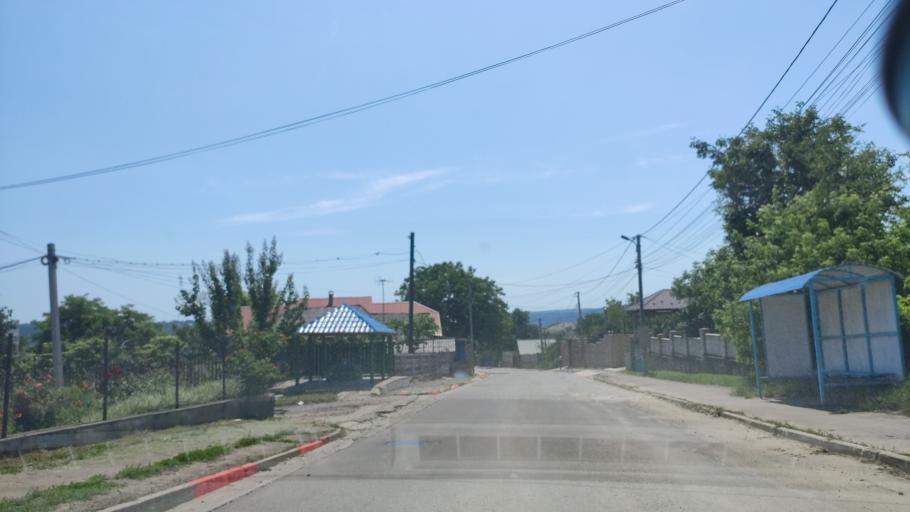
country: MD
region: Raionul Soroca
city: Soroca
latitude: 48.1697
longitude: 28.2990
